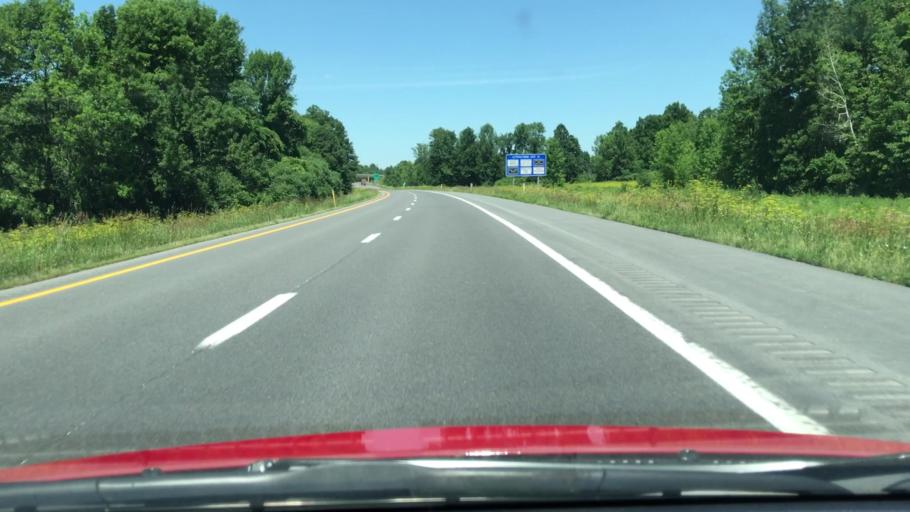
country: US
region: New York
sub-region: Clinton County
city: Champlain
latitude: 44.8642
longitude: -73.4494
